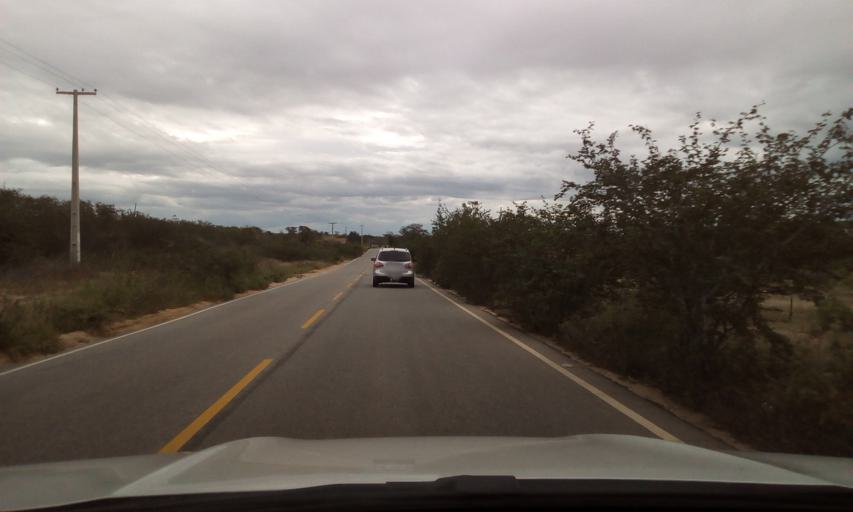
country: BR
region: Paraiba
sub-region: Picui
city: Picui
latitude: -6.5608
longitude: -36.2858
